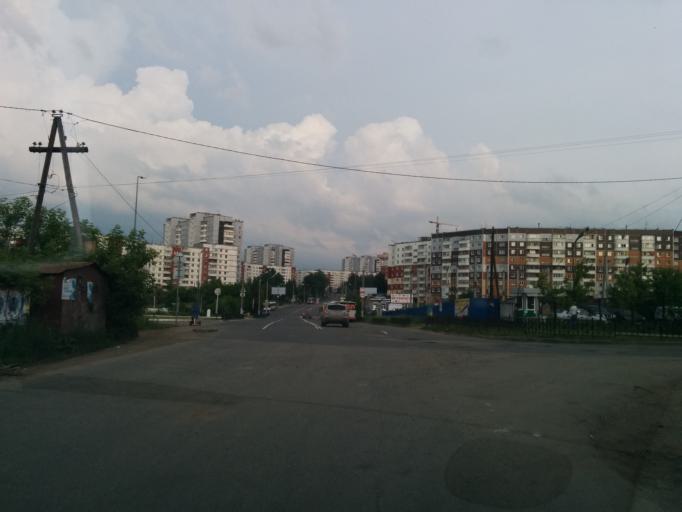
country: RU
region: Perm
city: Perm
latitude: 58.0135
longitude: 56.3049
